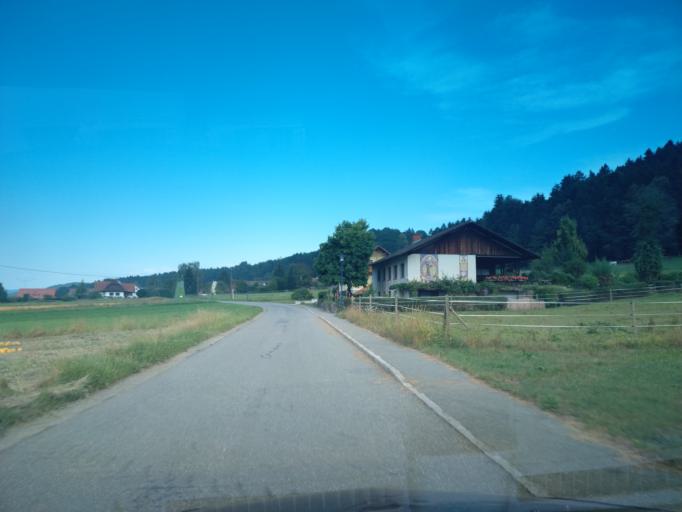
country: AT
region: Styria
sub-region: Politischer Bezirk Deutschlandsberg
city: Wies
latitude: 46.7167
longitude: 15.2770
